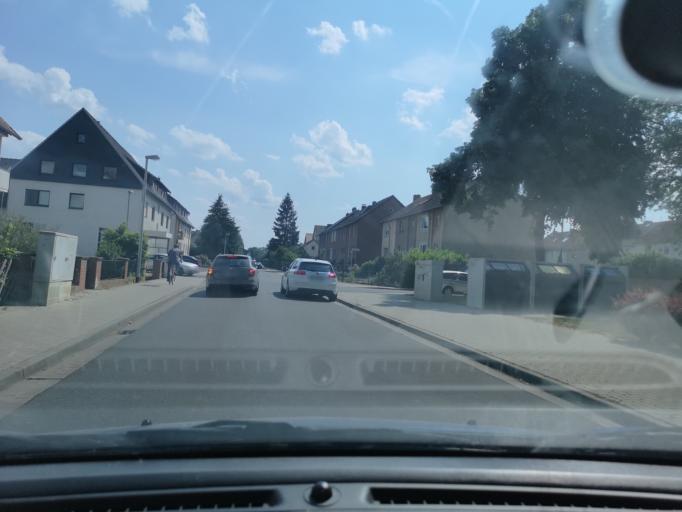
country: DE
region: Lower Saxony
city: Langenhagen
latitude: 52.4362
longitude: 9.7384
